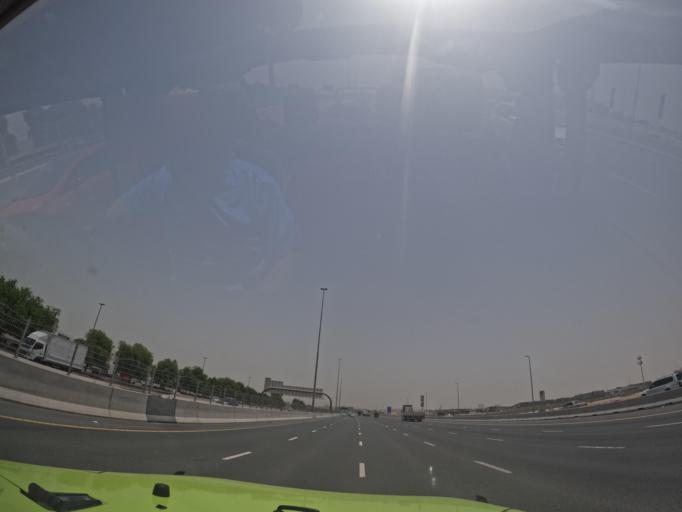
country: AE
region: Ash Shariqah
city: Sharjah
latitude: 25.1302
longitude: 55.3785
